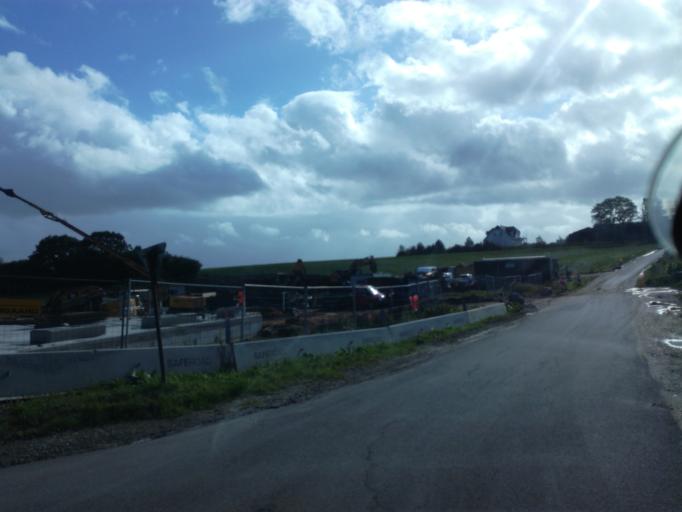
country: DK
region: South Denmark
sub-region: Vejle Kommune
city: Brejning
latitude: 55.6353
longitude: 9.7178
